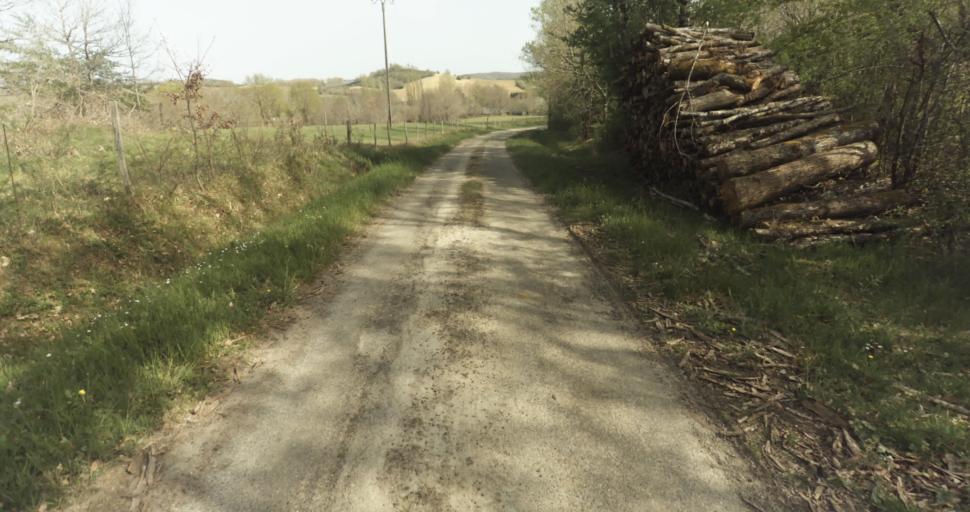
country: FR
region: Midi-Pyrenees
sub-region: Departement du Tarn-et-Garonne
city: Lafrancaise
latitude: 44.1480
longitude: 1.1751
